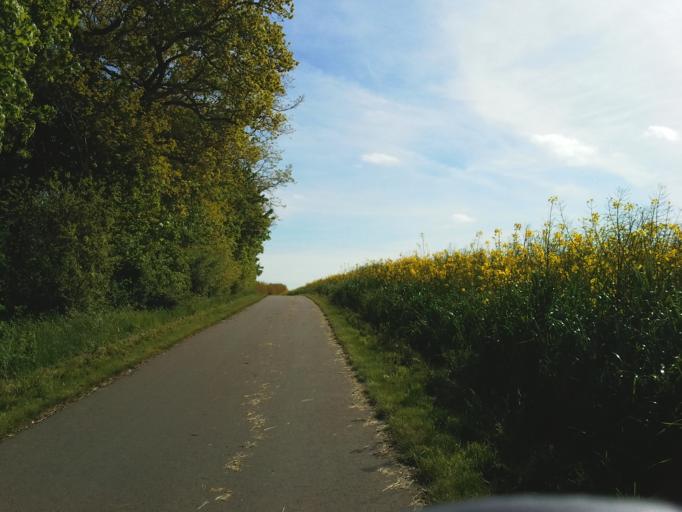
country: DE
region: Mecklenburg-Vorpommern
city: Schwaan
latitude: 53.9829
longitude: 12.1048
